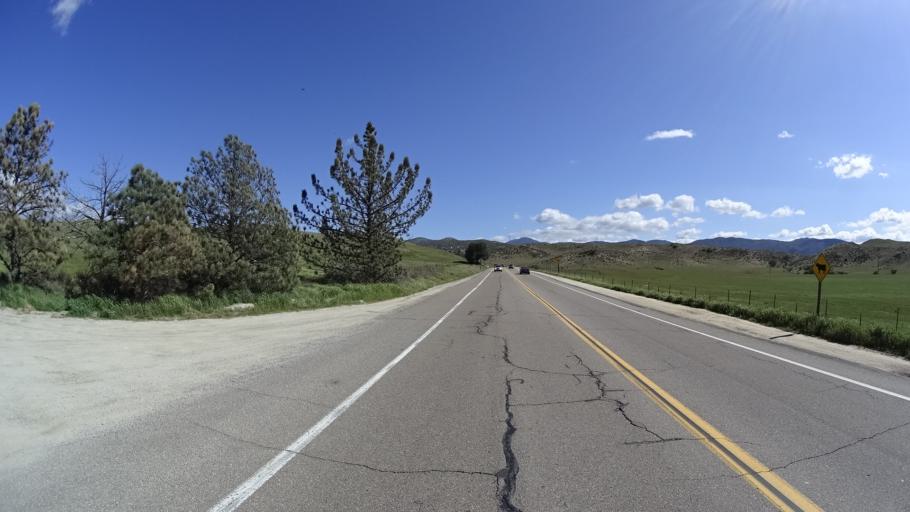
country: US
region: California
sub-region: San Diego County
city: Julian
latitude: 33.2485
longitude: -116.6734
